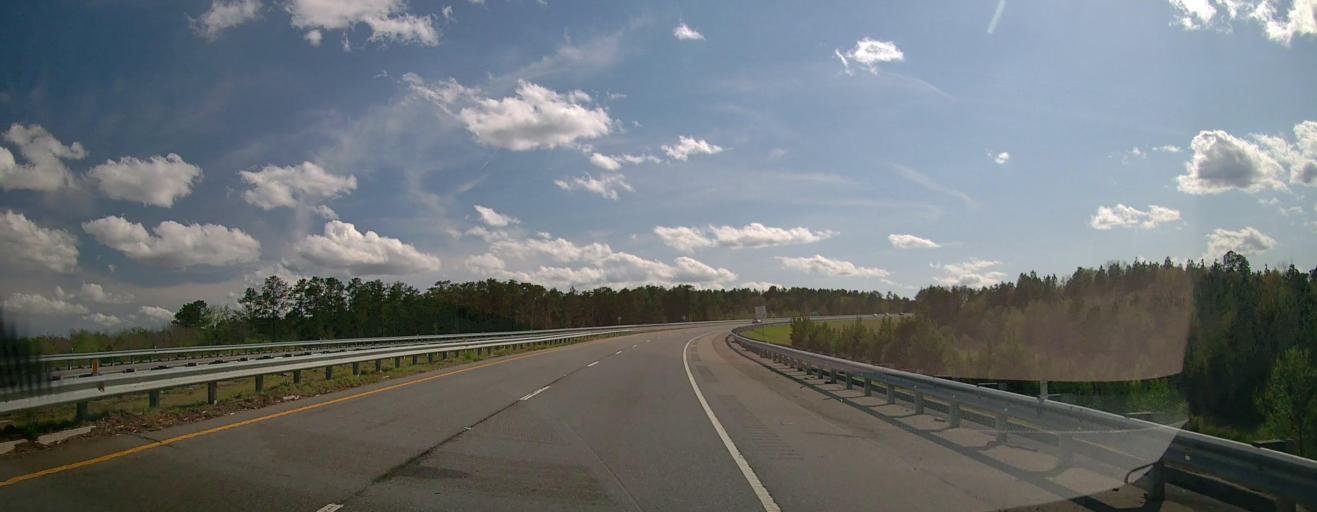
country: US
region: Georgia
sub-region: Baldwin County
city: Hardwick
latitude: 32.9839
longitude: -83.2066
